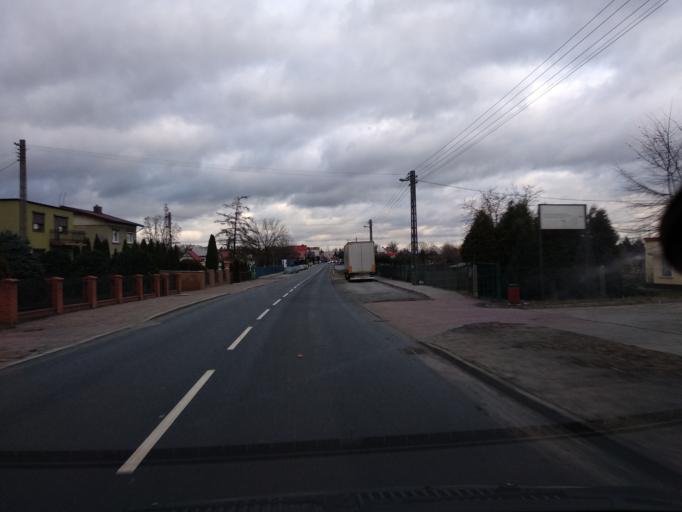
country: PL
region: Lower Silesian Voivodeship
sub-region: Powiat olesnicki
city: Miedzyborz
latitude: 51.3995
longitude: 17.6667
